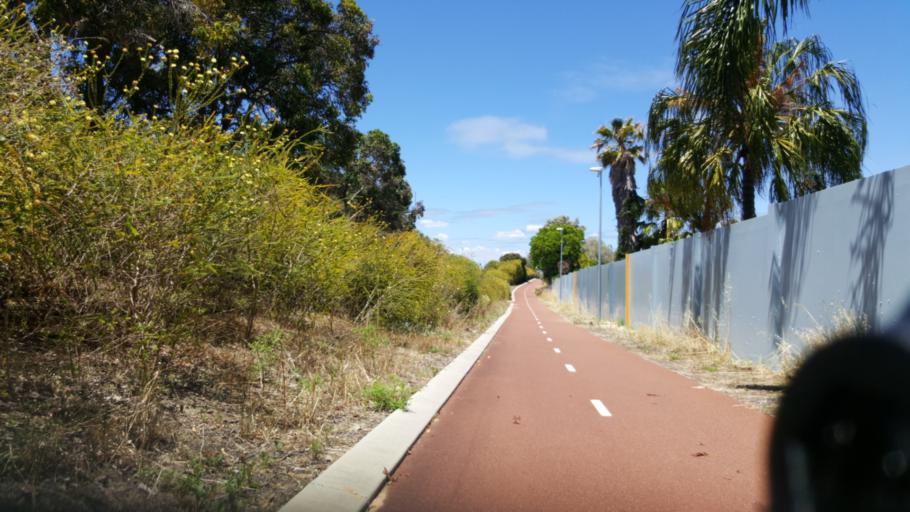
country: AU
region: Western Australia
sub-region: Stirling
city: Westminster
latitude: -31.8687
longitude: 115.8813
